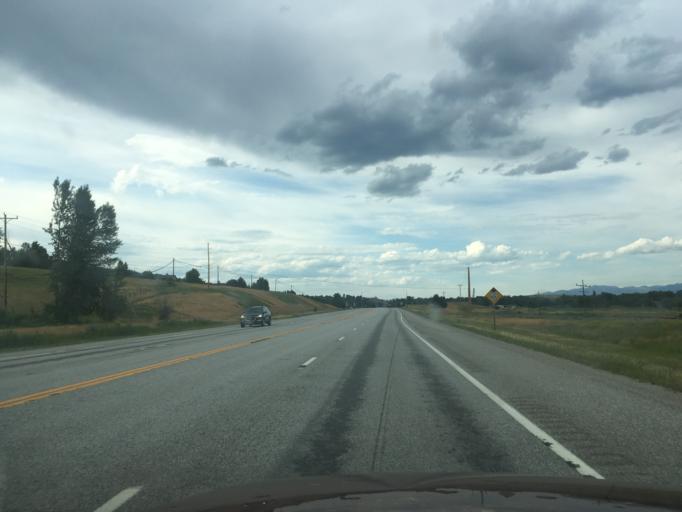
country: US
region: Montana
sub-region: Missoula County
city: Lolo
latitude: 46.7374
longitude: -114.0807
